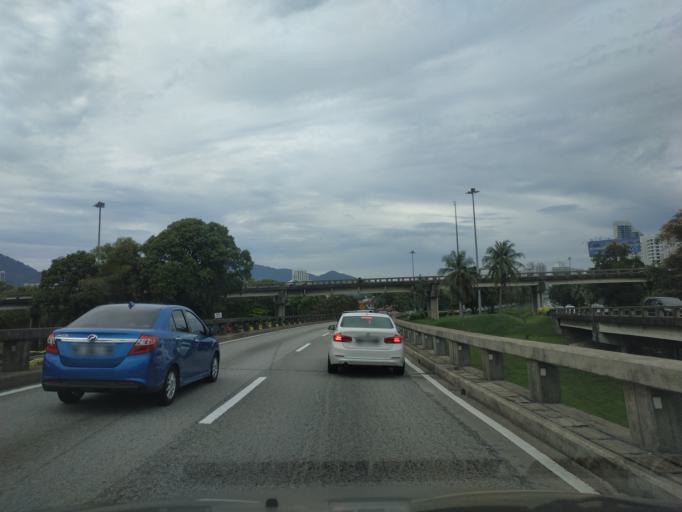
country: MY
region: Penang
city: Kampung Sungai Ara
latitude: 5.3602
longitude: 100.3146
